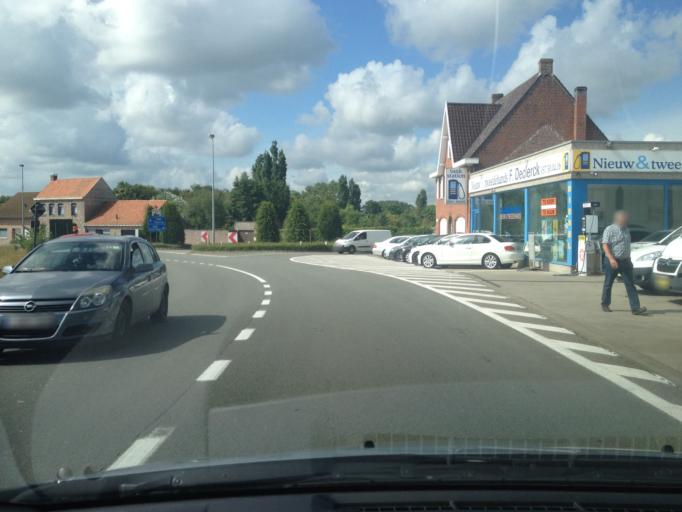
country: FR
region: Nord-Pas-de-Calais
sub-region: Departement du Nord
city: Hondschoote
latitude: 50.9247
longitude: 2.6179
